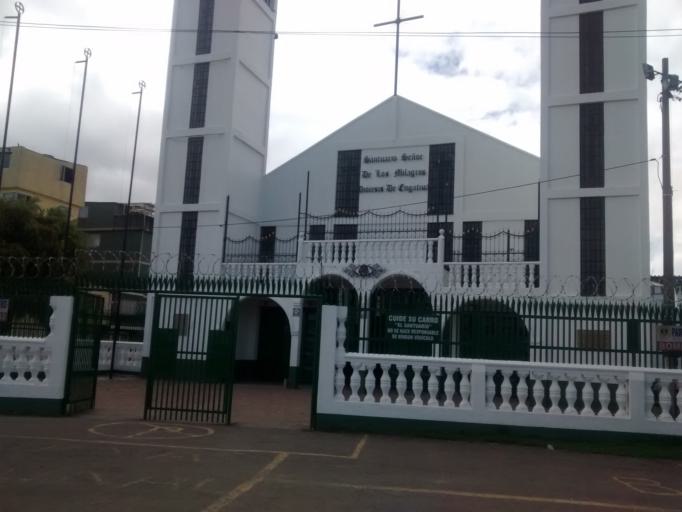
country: CO
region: Bogota D.C.
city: Barrio San Luis
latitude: 4.7105
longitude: -74.1084
